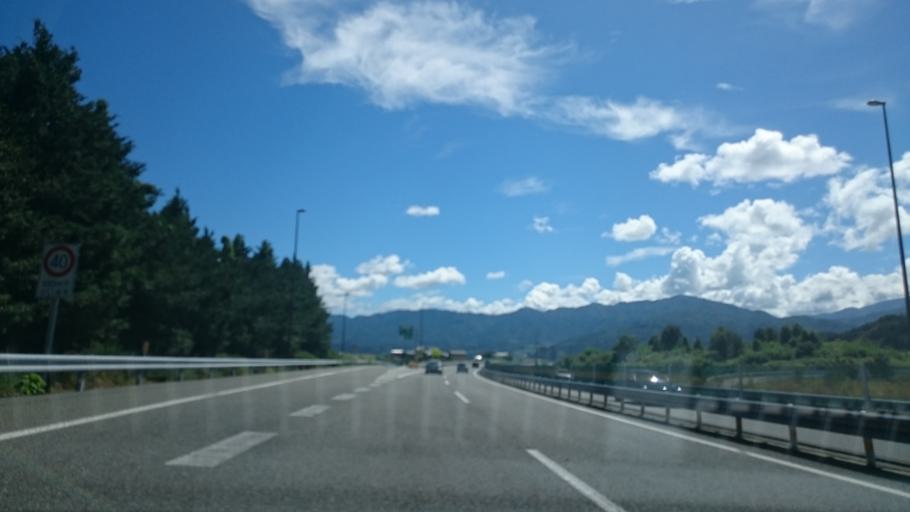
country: JP
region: Nagano
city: Iida
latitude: 35.4708
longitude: 137.7593
